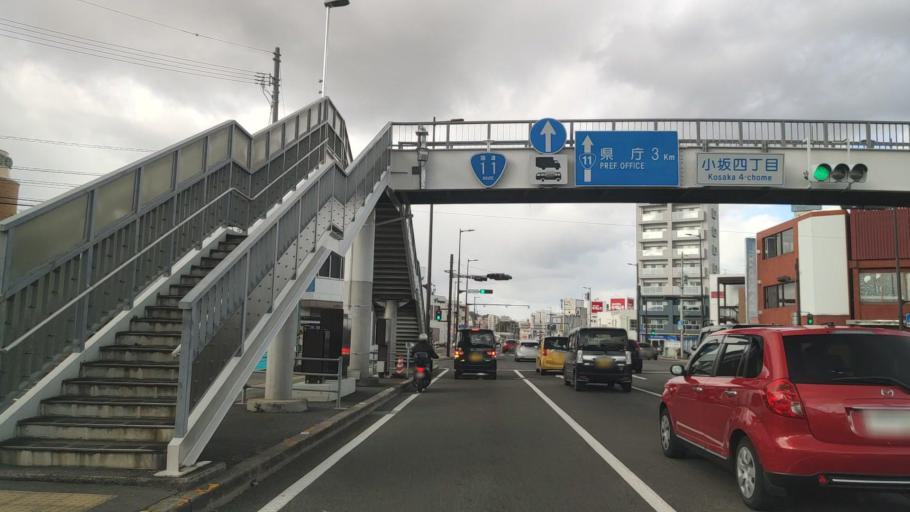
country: JP
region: Ehime
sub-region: Shikoku-chuo Shi
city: Matsuyama
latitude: 33.8293
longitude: 132.7810
